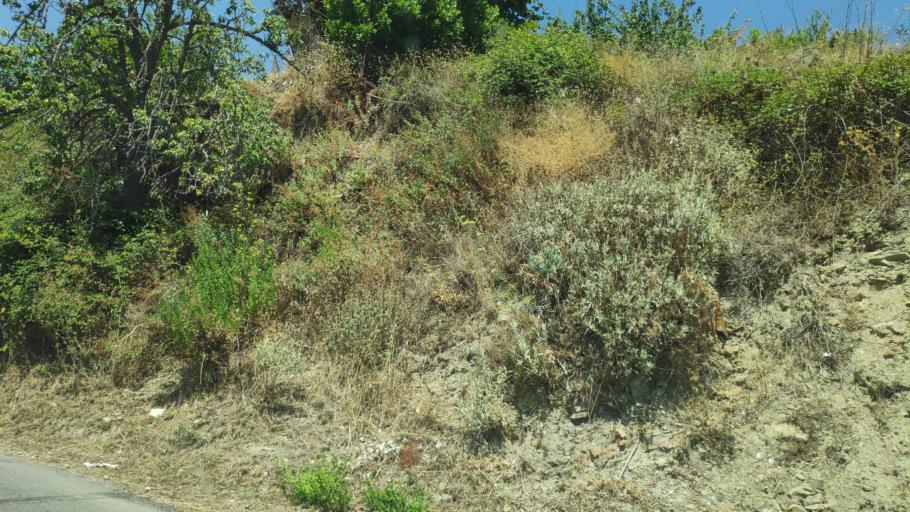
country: IT
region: Calabria
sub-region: Provincia di Reggio Calabria
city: Bova
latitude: 37.9926
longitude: 15.9308
